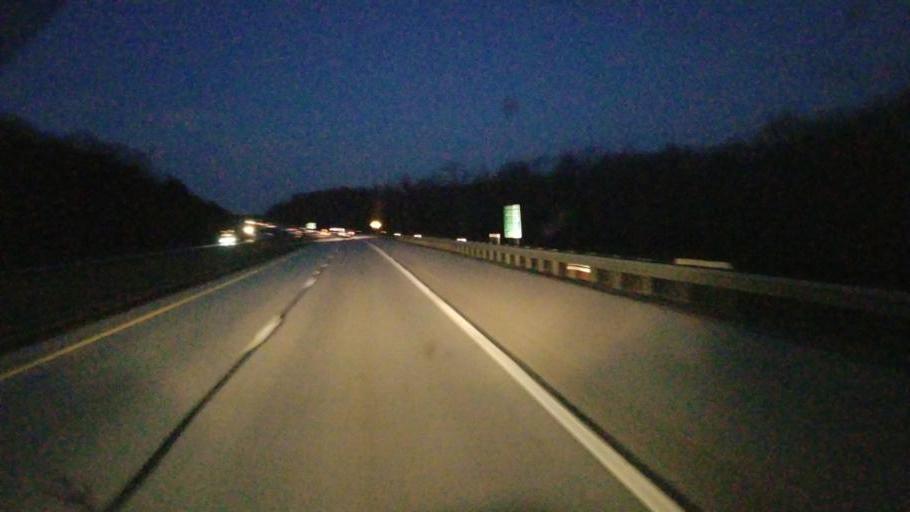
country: US
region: Ohio
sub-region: Ashtabula County
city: Edgewood
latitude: 41.8431
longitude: -80.7212
